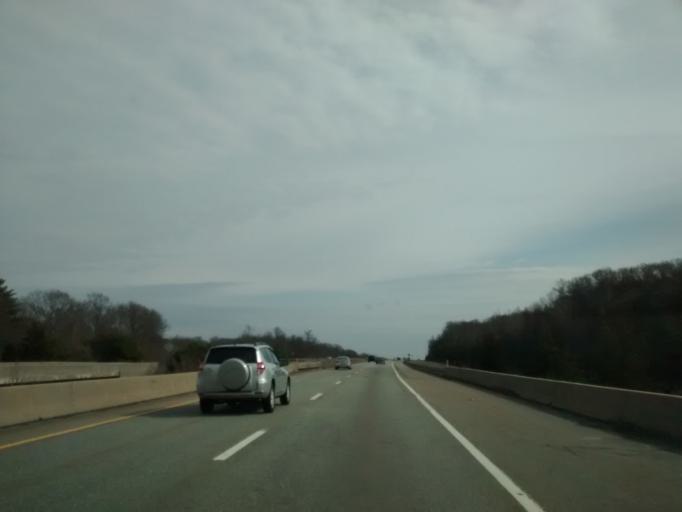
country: US
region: Massachusetts
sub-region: Worcester County
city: Uxbridge
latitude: 42.0463
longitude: -71.6283
